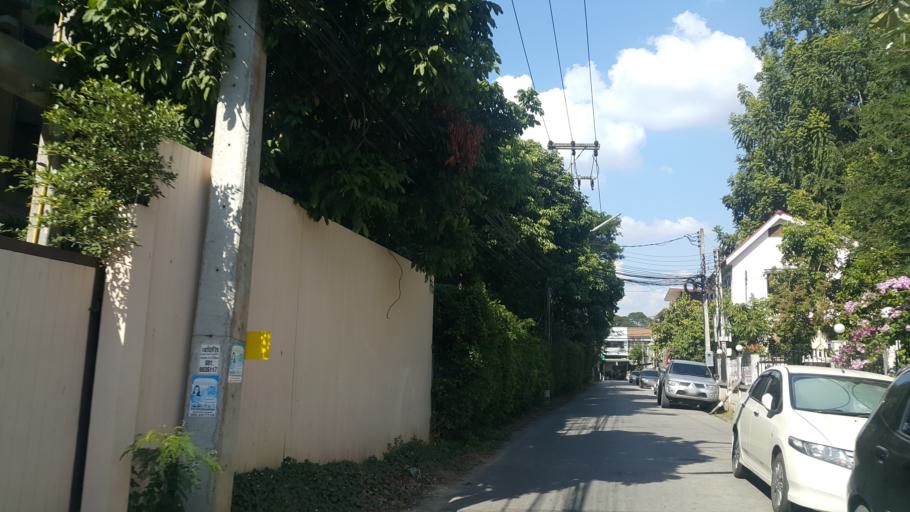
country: TH
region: Chiang Mai
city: Chiang Mai
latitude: 18.7729
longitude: 99.0158
